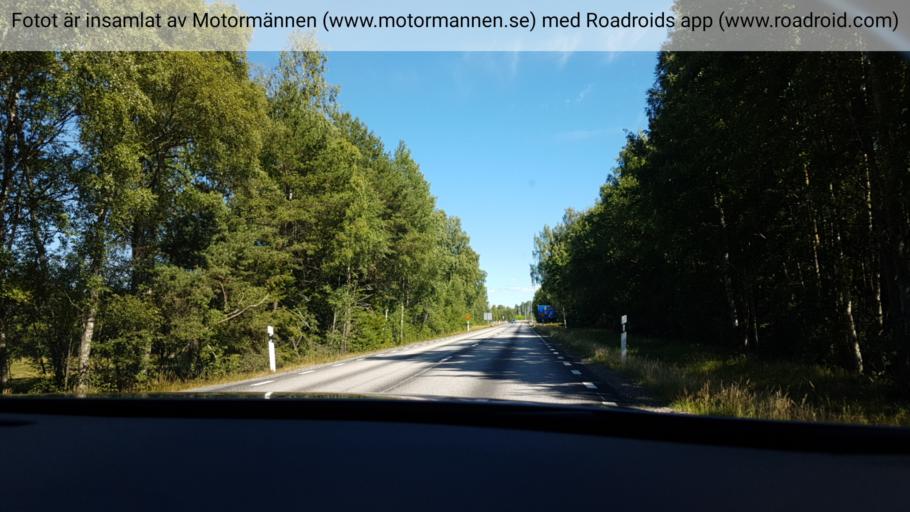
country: SE
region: Joenkoeping
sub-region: Gnosjo Kommun
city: Hillerstorp
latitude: 57.3172
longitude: 13.9027
